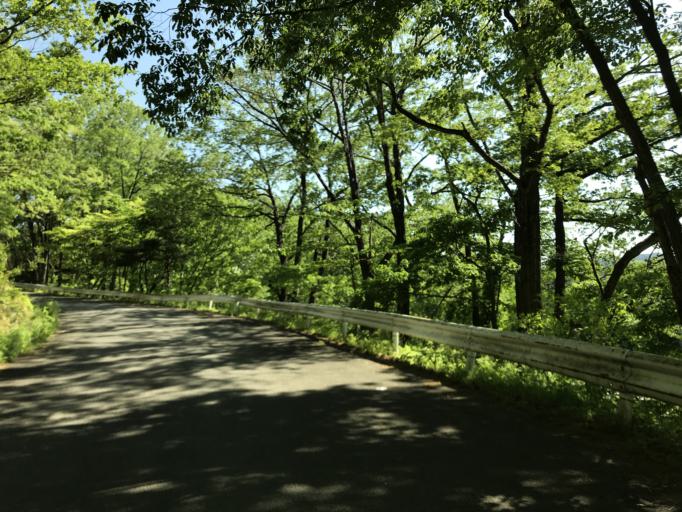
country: JP
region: Fukushima
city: Yanagawamachi-saiwaicho
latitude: 37.7581
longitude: 140.6889
